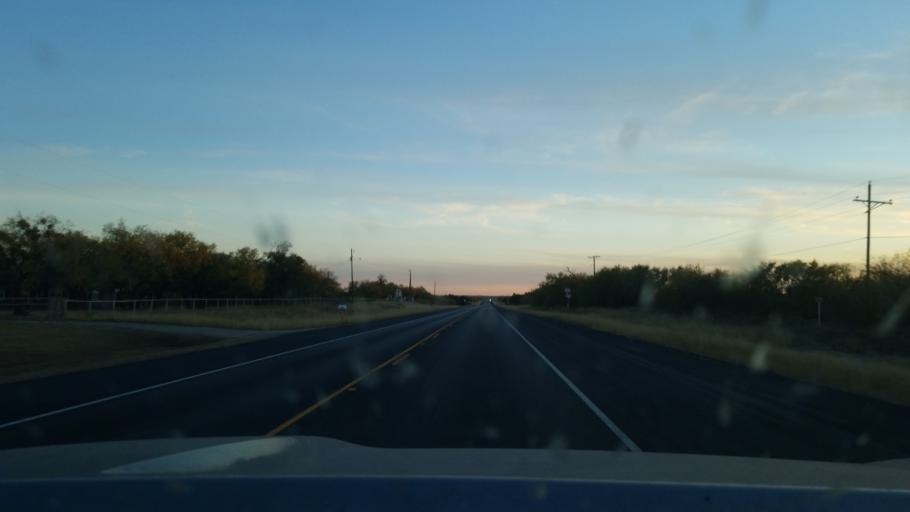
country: US
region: Texas
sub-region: Stephens County
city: Breckenridge
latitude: 32.6778
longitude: -98.9021
